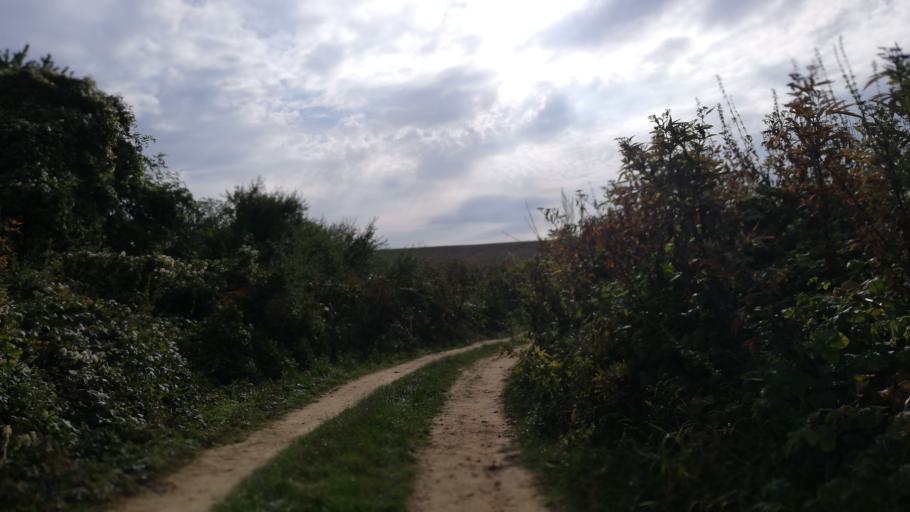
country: CZ
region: South Moravian
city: Sudomerice
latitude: 48.8175
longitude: 17.2790
